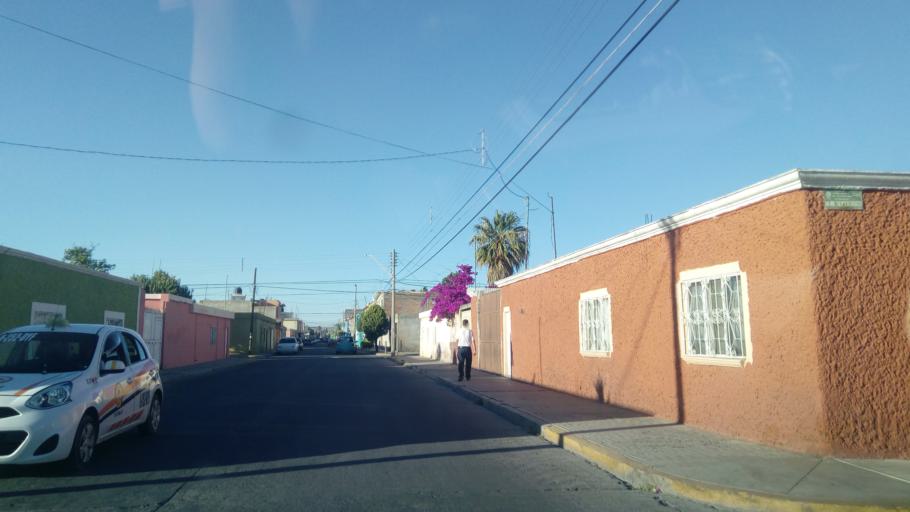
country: MX
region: Durango
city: Victoria de Durango
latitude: 24.0031
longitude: -104.6738
